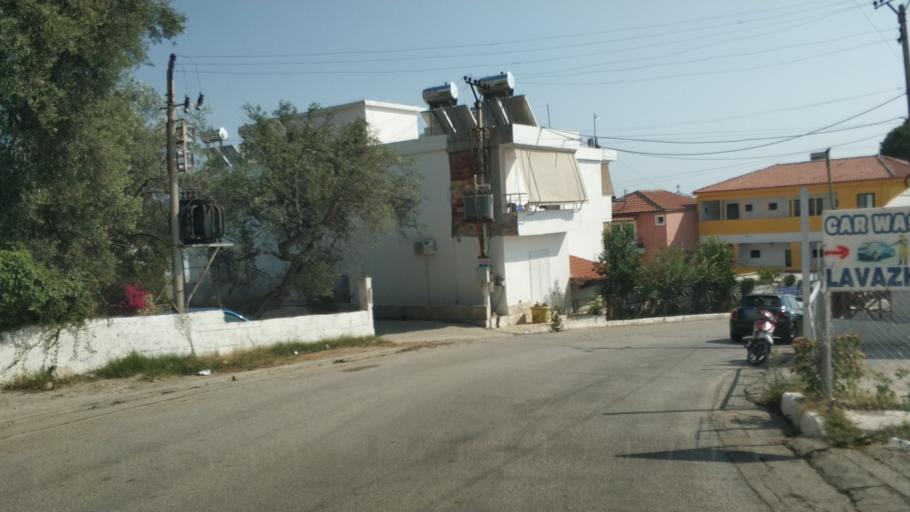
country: AL
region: Vlore
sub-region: Rrethi i Vlores
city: Vranisht
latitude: 40.1465
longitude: 19.6344
